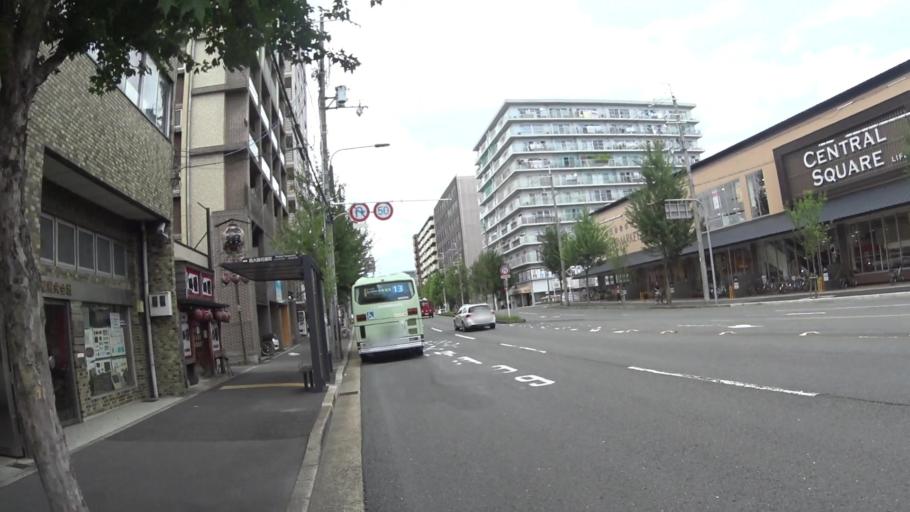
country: JP
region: Kyoto
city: Kyoto
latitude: 34.9929
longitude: 135.7322
